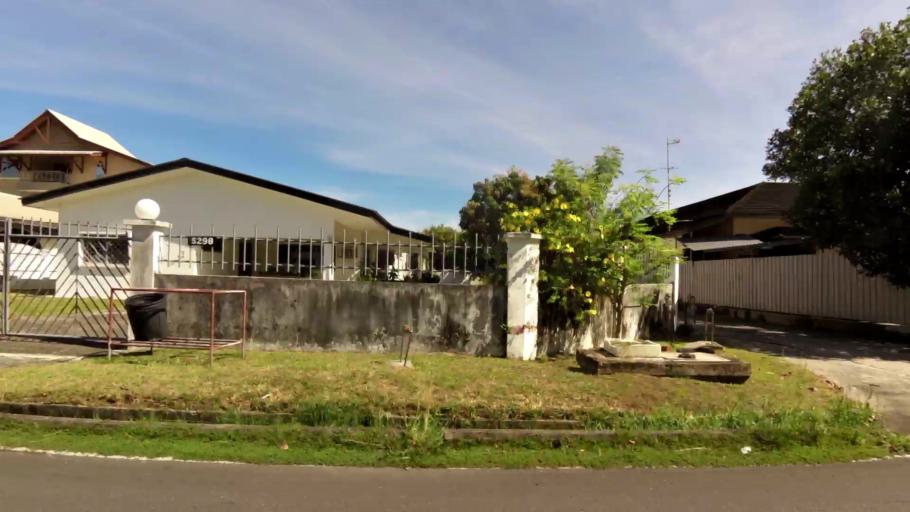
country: BN
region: Belait
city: Kuala Belait
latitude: 4.5855
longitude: 114.2036
